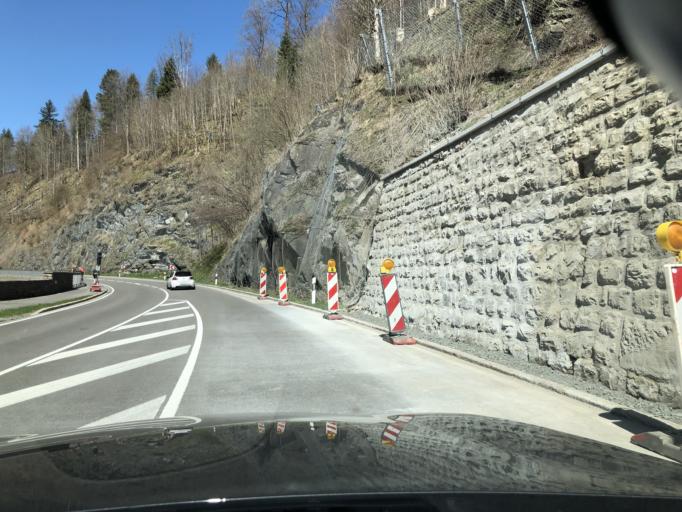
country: DE
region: Bavaria
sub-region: Swabia
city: Wertach
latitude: 47.5817
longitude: 10.4203
